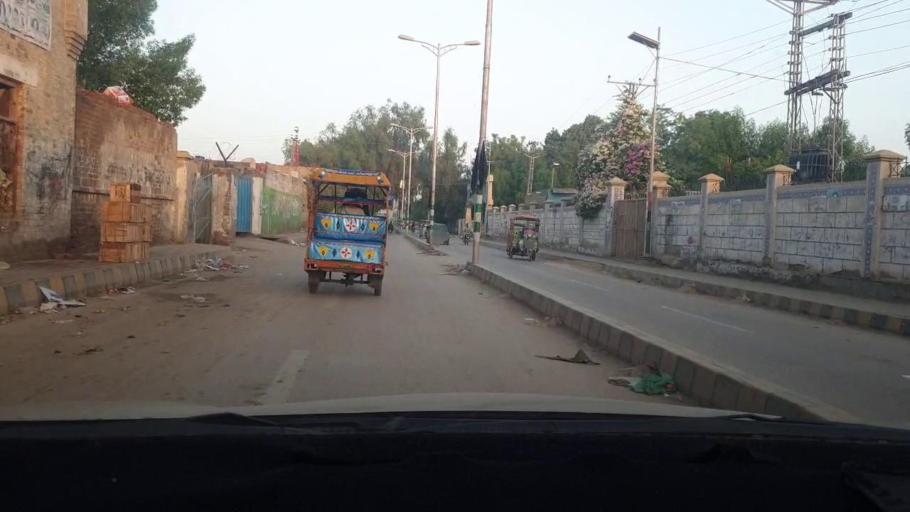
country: PK
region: Sindh
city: Larkana
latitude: 27.5575
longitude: 68.2119
